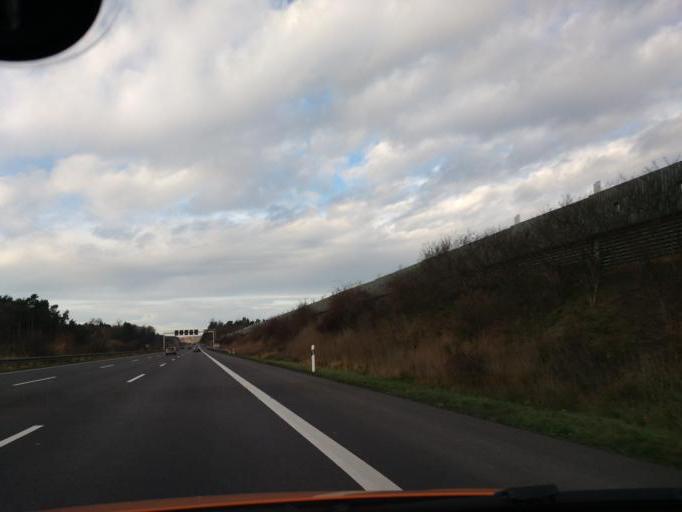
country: DE
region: Lower Saxony
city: Rennau
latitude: 52.2885
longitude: 10.8896
